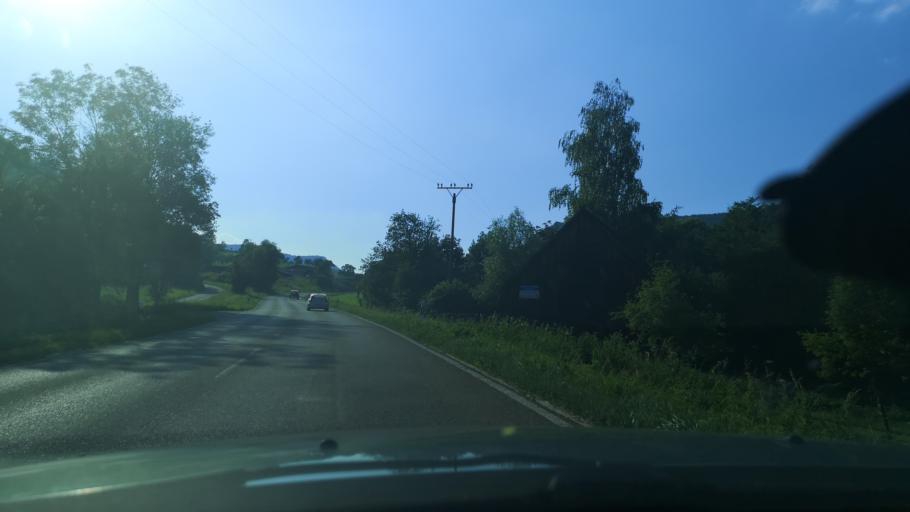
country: DE
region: Baden-Wuerttemberg
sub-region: Regierungsbezirk Stuttgart
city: Deggingen
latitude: 48.6237
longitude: 9.7254
